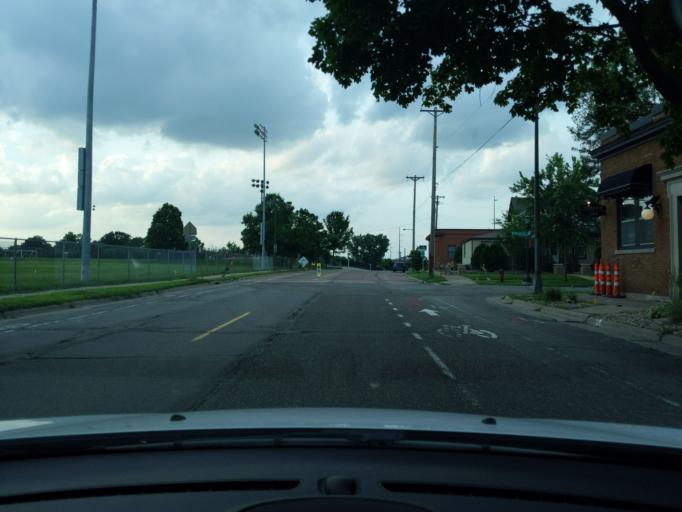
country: US
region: Minnesota
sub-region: Ramsey County
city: Falcon Heights
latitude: 44.9513
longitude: -93.1827
